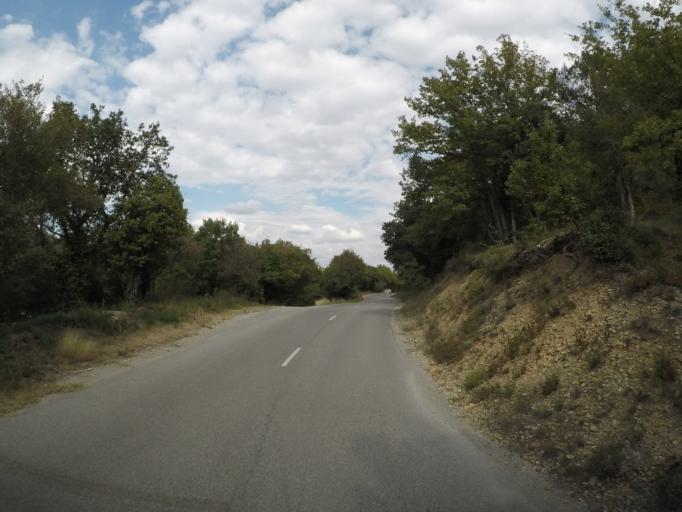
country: FR
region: Provence-Alpes-Cote d'Azur
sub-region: Departement des Alpes-de-Haute-Provence
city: Valensole
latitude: 43.8175
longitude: 5.9637
